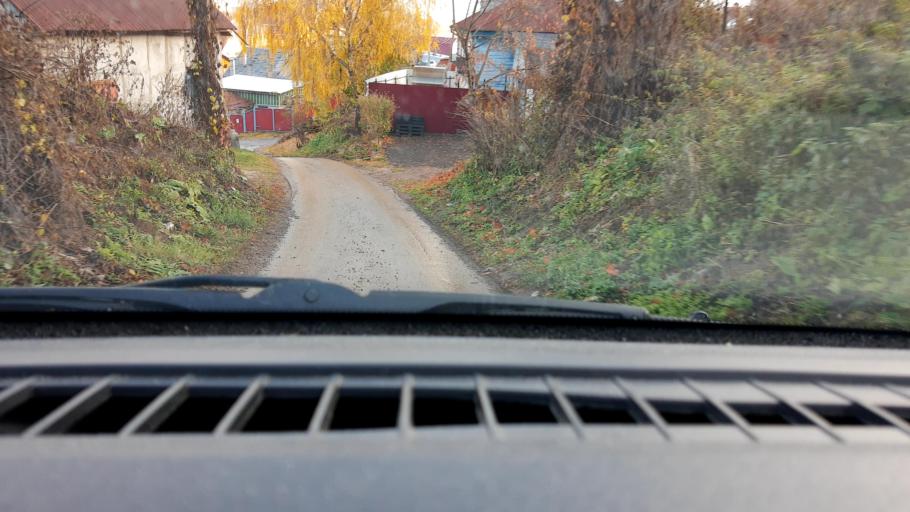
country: RU
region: Nizjnij Novgorod
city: Afonino
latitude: 56.3004
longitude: 44.0980
